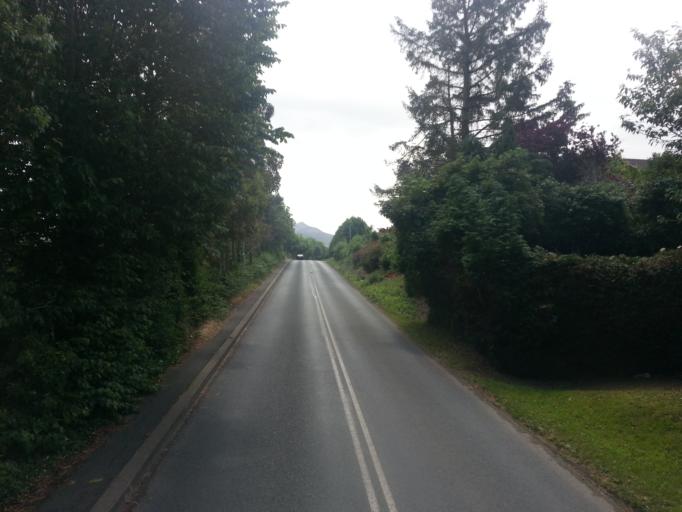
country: IE
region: Leinster
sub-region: Wicklow
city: Enniskerry
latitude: 53.2103
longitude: -6.1752
